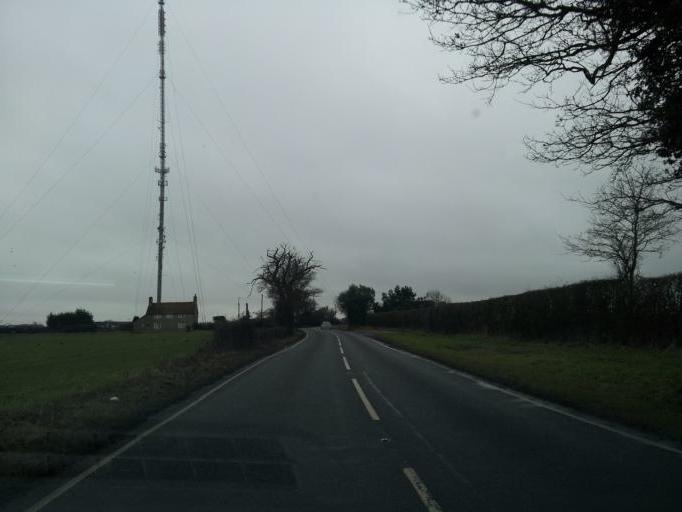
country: GB
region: England
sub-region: Essex
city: Mistley
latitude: 51.9263
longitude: 1.0846
